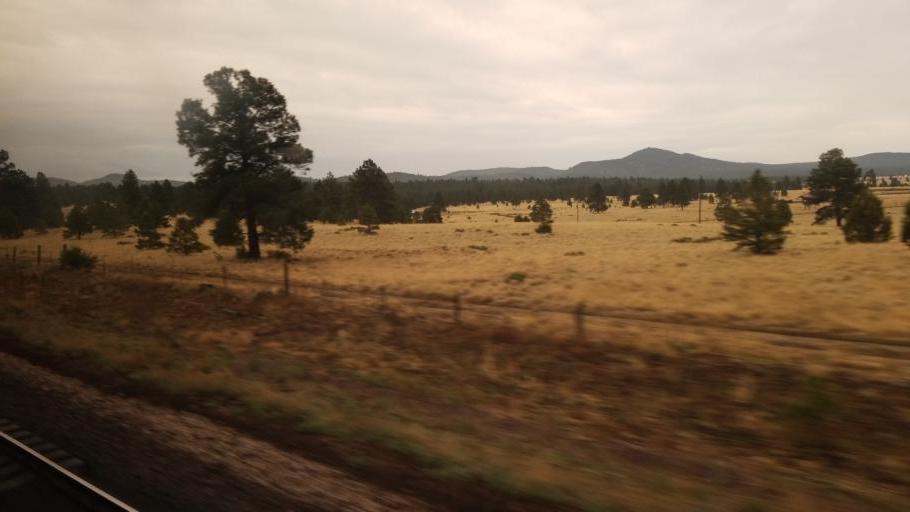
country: US
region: Arizona
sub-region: Coconino County
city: Parks
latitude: 35.2441
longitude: -111.9731
